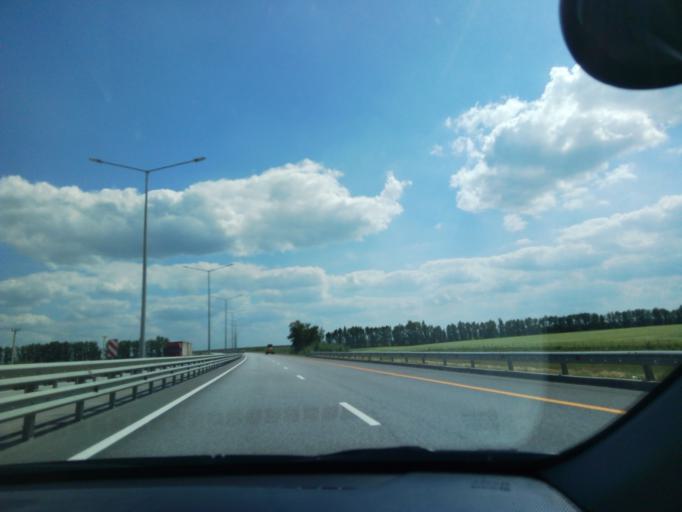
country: RU
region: Voronezj
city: Podkletnoye
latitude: 51.5191
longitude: 39.5108
